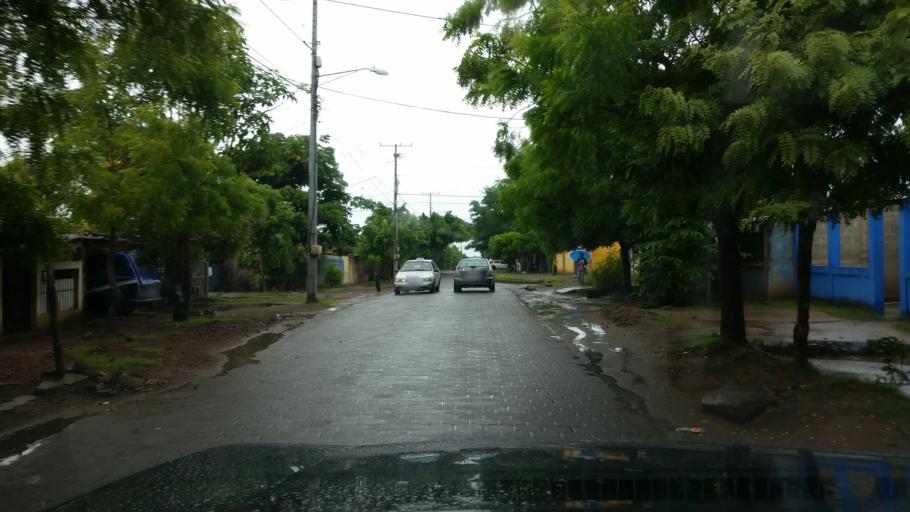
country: NI
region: Granada
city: Granada
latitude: 11.9237
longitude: -85.9512
